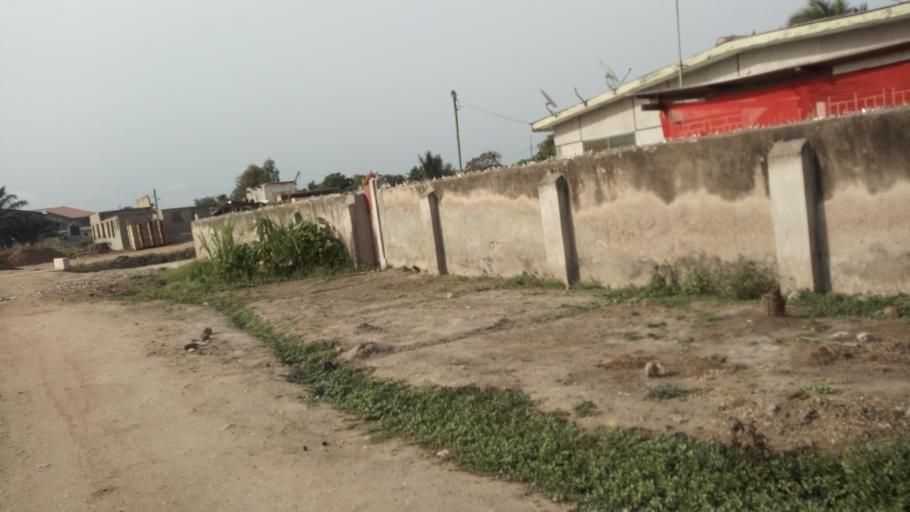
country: GH
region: Central
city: Winneba
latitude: 5.3488
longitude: -0.6340
